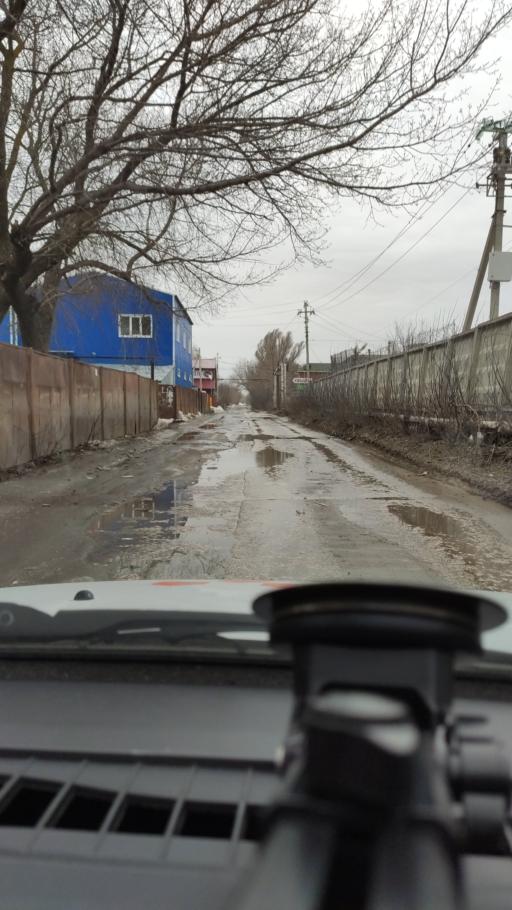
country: RU
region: Samara
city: Tol'yatti
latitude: 53.5364
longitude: 49.2598
